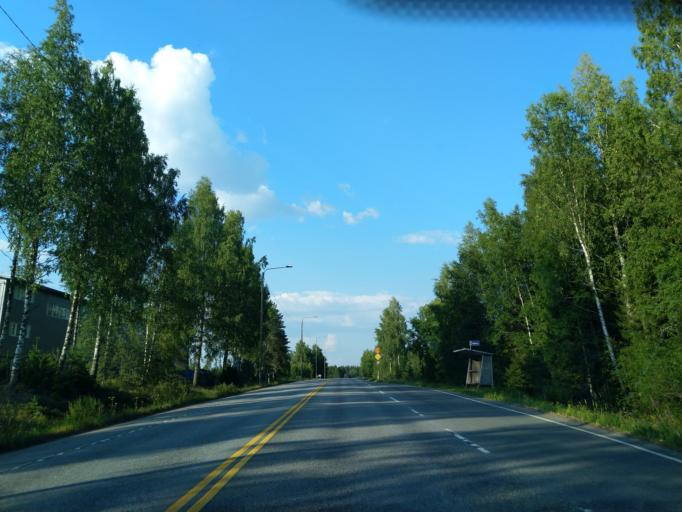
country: FI
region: Satakunta
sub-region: Pori
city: Laengelmaeki
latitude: 61.7590
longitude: 22.1372
